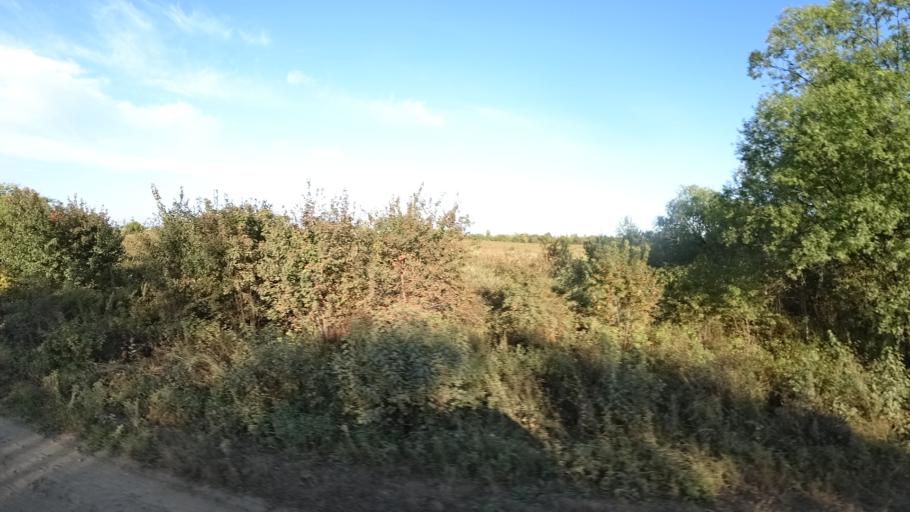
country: RU
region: Amur
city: Arkhara
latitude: 49.3669
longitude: 130.1361
